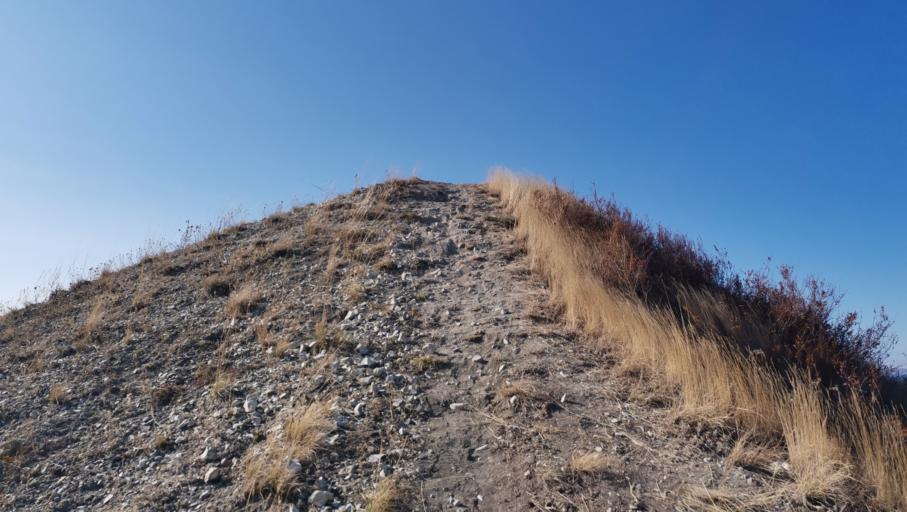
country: RU
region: Ulyanovsk
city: Novoul'yanovsk
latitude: 54.1131
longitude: 48.5657
